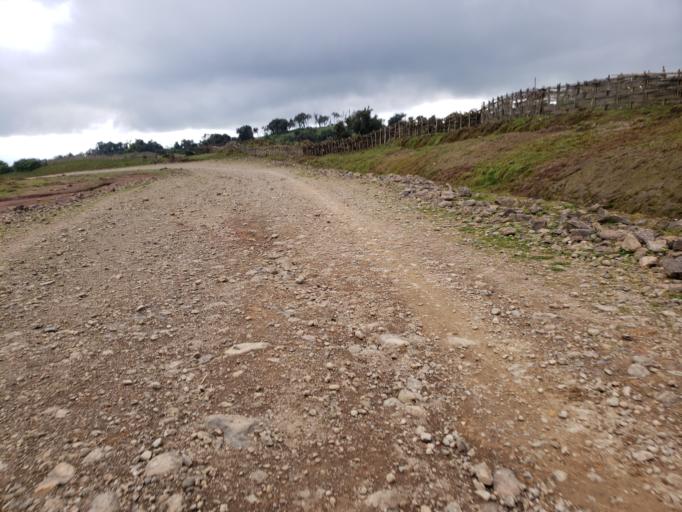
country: ET
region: Oromiya
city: Dodola
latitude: 6.6971
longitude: 39.3697
